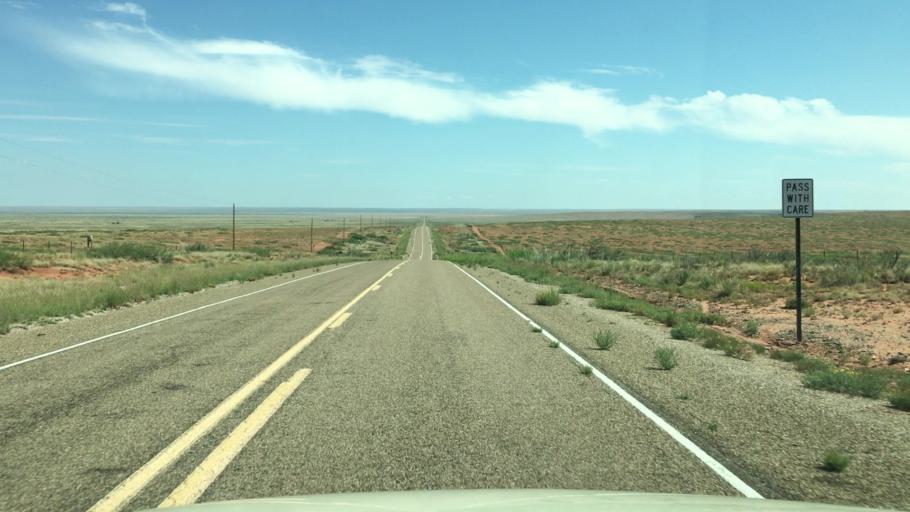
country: US
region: New Mexico
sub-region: Chaves County
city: Roswell
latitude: 33.9708
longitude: -104.5792
